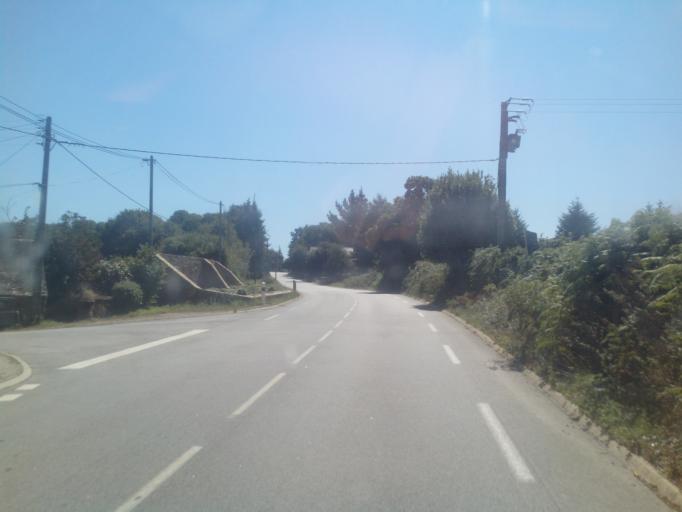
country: FR
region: Brittany
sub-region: Departement du Morbihan
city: Guegon
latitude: 47.9059
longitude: -2.5210
